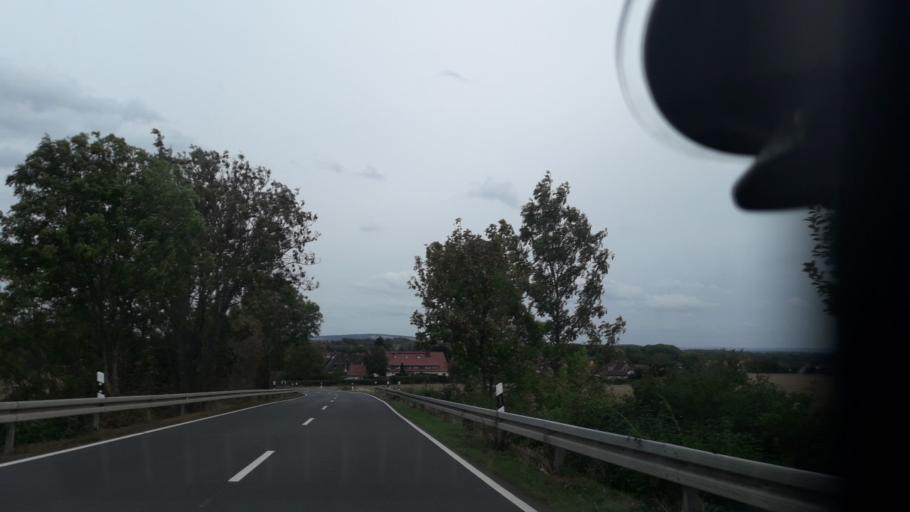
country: DE
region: Lower Saxony
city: Heiningen
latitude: 52.0717
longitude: 10.5486
